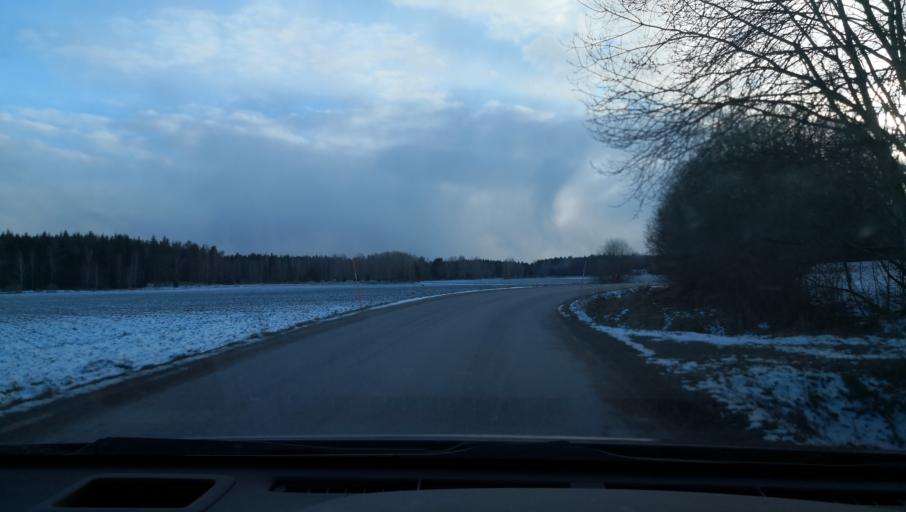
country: SE
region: Vaestmanland
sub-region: Vasteras
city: Tillberga
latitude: 59.6417
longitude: 16.7410
